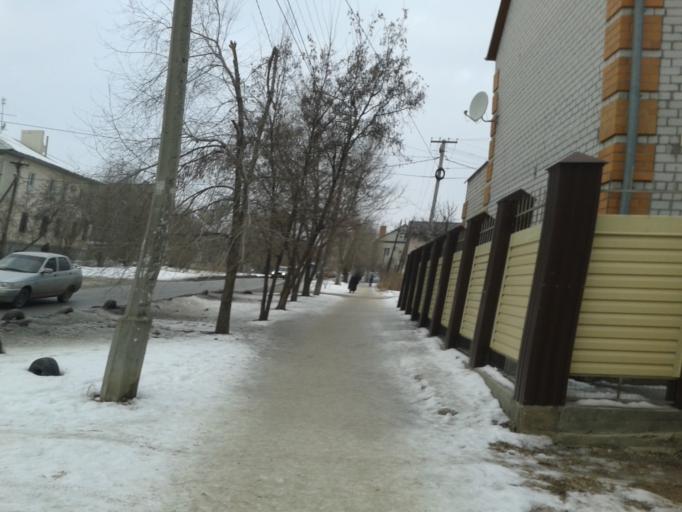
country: RU
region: Volgograd
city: Volgograd
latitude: 48.7235
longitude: 44.5100
